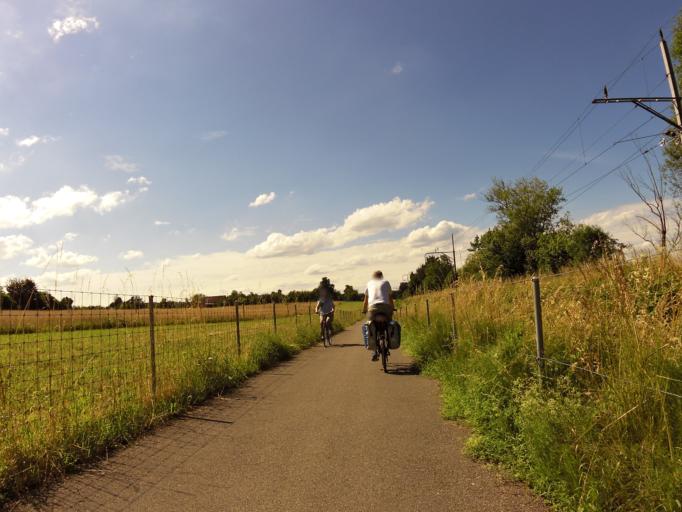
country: CH
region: Thurgau
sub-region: Arbon District
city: Arbon
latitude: 47.5286
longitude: 9.4141
